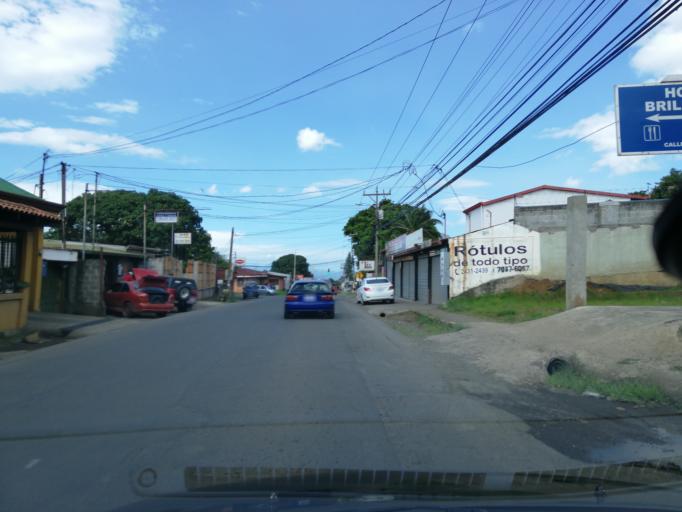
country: CR
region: Alajuela
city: Alajuela
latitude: 9.9909
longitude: -84.2376
